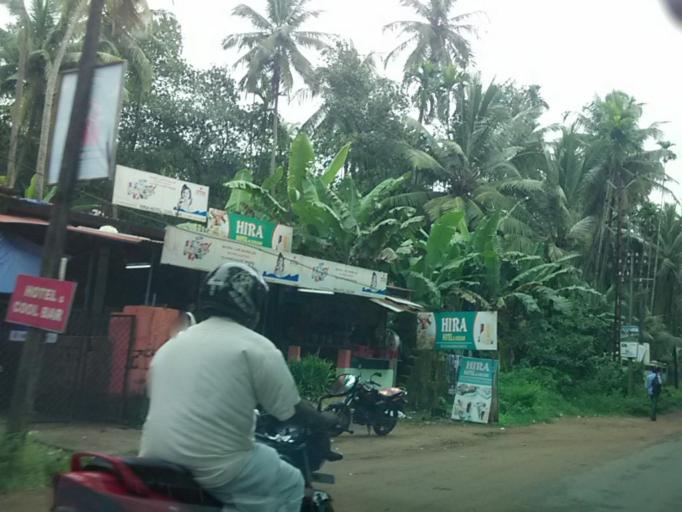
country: IN
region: Kerala
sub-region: Kozhikode
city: Kunnamangalam
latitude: 11.3142
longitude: 75.9246
